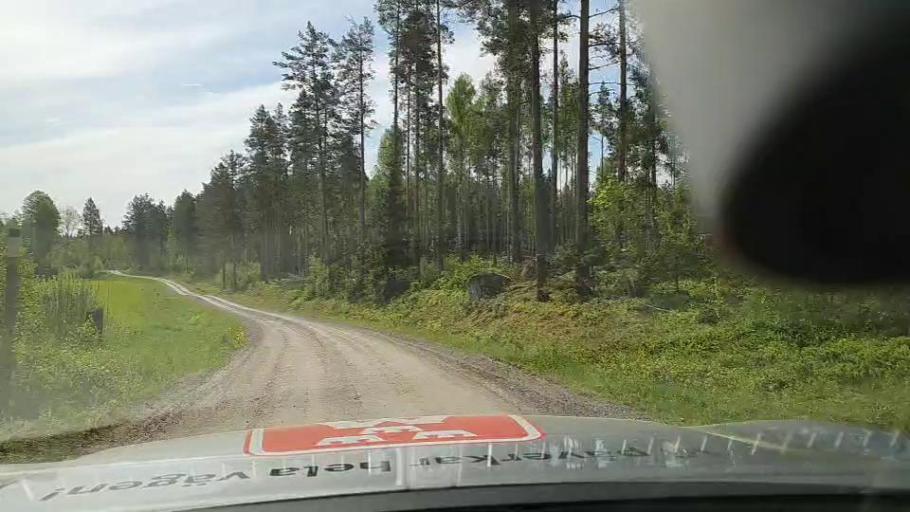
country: SE
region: Soedermanland
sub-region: Eskilstuna Kommun
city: Arla
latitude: 59.2626
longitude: 16.8215
